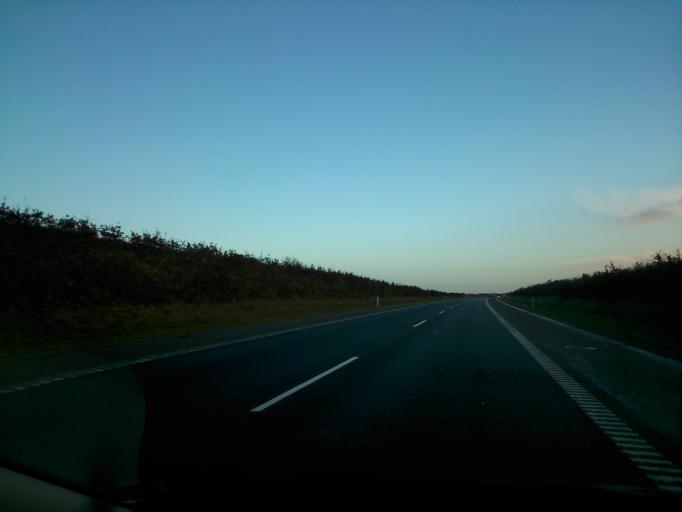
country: DK
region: Central Jutland
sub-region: Herning Kommune
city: Snejbjerg
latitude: 56.1238
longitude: 8.8911
